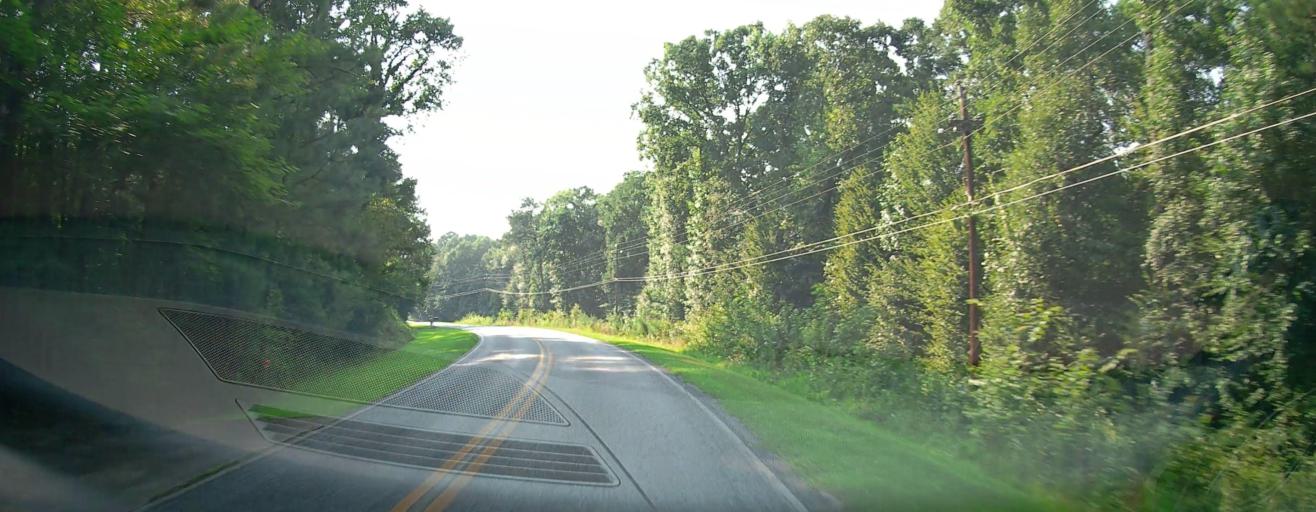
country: US
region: Georgia
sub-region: Bibb County
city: Macon
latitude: 32.9554
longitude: -83.7328
